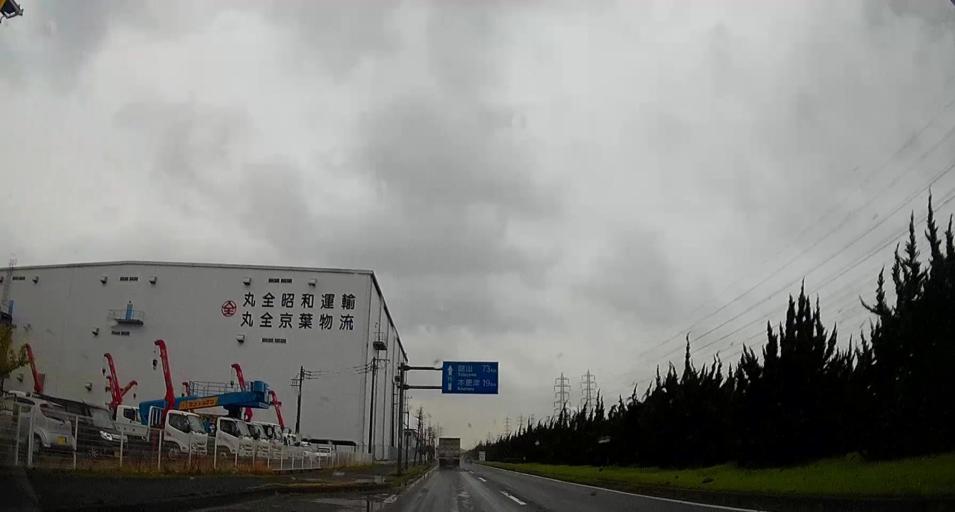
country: JP
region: Chiba
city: Ichihara
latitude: 35.4830
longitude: 140.0375
